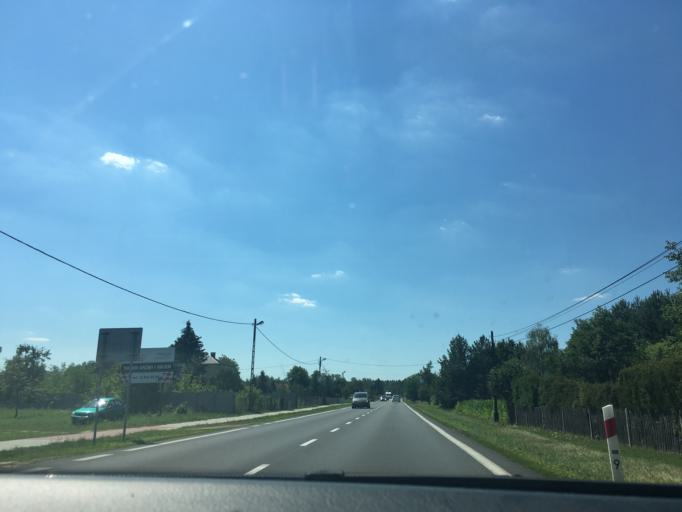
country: PL
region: Subcarpathian Voivodeship
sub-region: Powiat nizanski
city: Nisko
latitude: 50.5039
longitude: 22.1408
